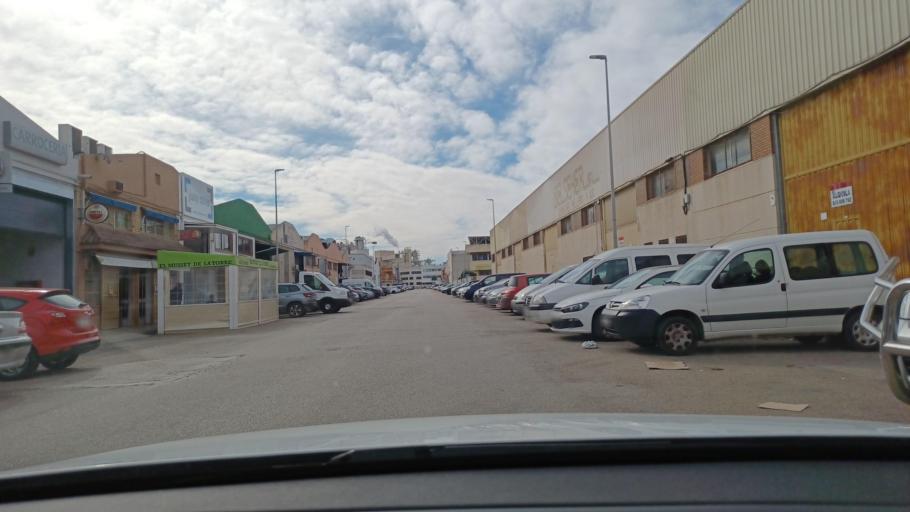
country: ES
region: Valencia
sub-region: Provincia de Valencia
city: Benifaio
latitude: 39.2875
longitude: -0.4323
